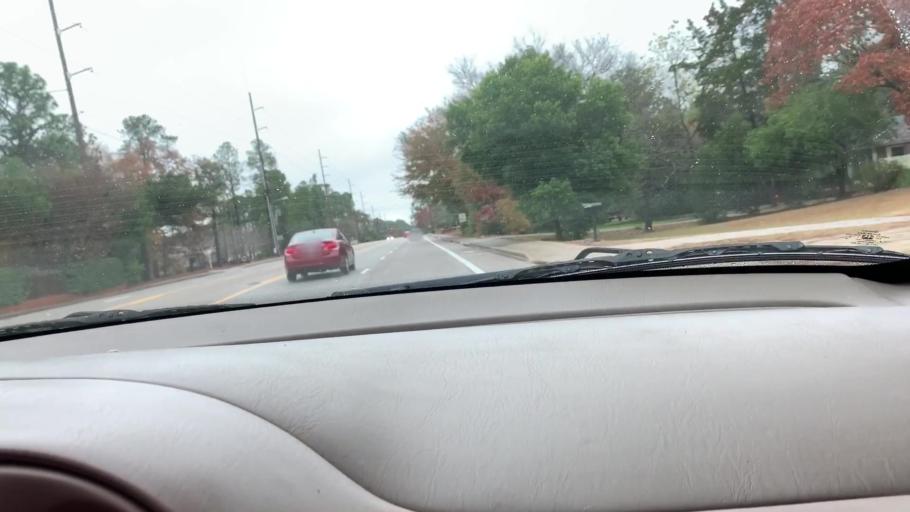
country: US
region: South Carolina
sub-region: Richland County
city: Dentsville
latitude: 34.0448
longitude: -80.9615
